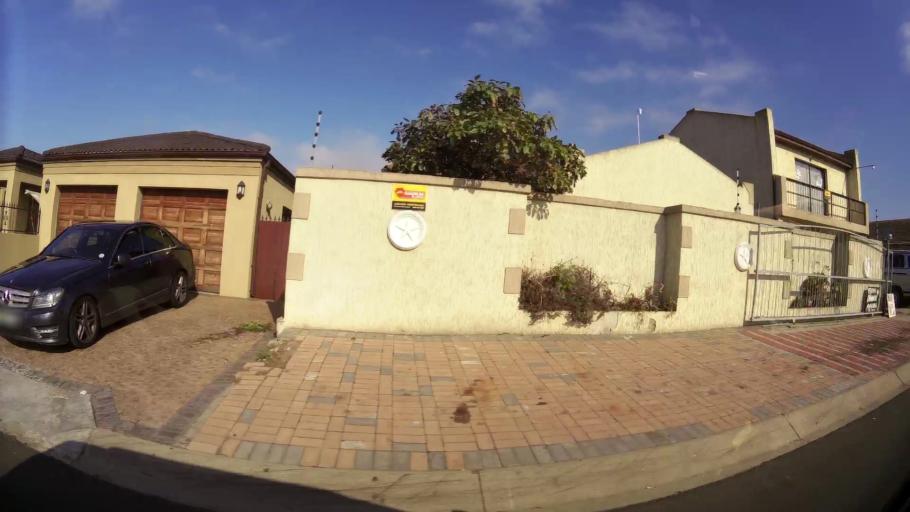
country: ZA
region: Eastern Cape
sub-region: Nelson Mandela Bay Metropolitan Municipality
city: Port Elizabeth
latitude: -33.9226
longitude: 25.5310
